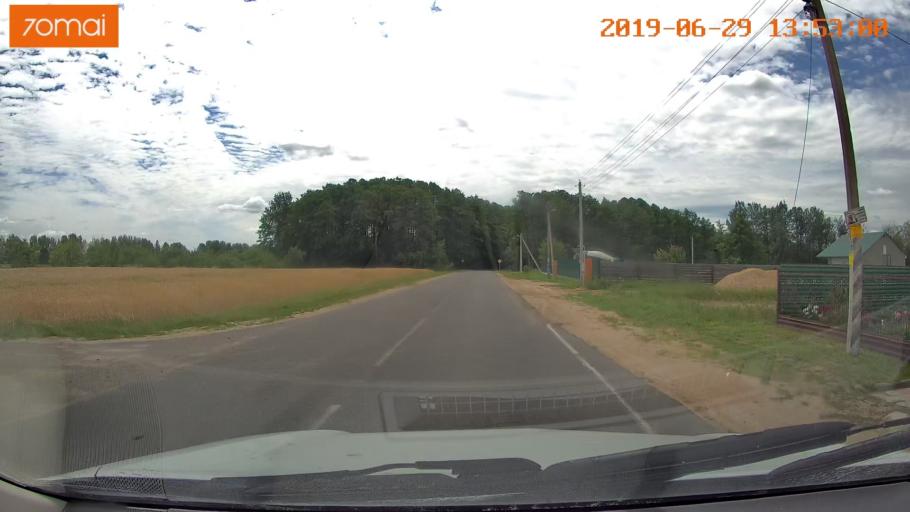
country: BY
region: Minsk
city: Slutsk
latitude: 52.9917
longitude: 27.5495
